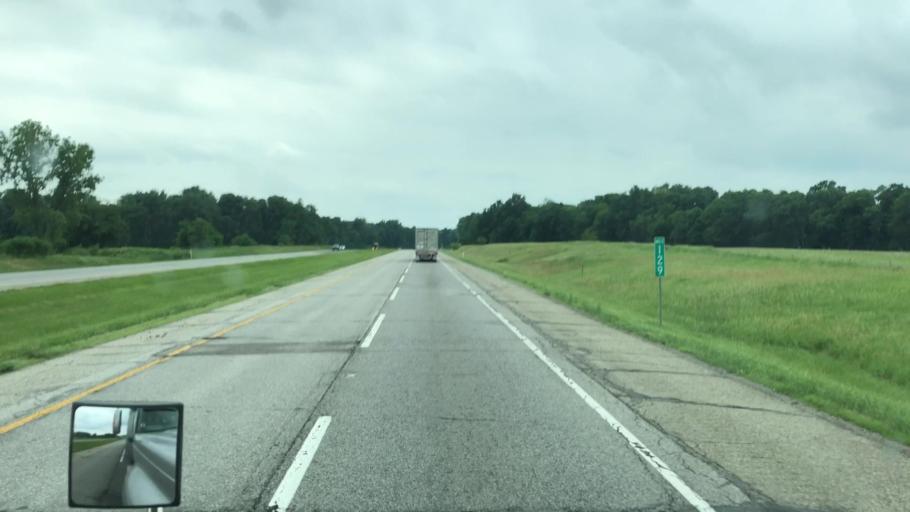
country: US
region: Michigan
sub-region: Branch County
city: Bronson
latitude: 41.7472
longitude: -85.2728
